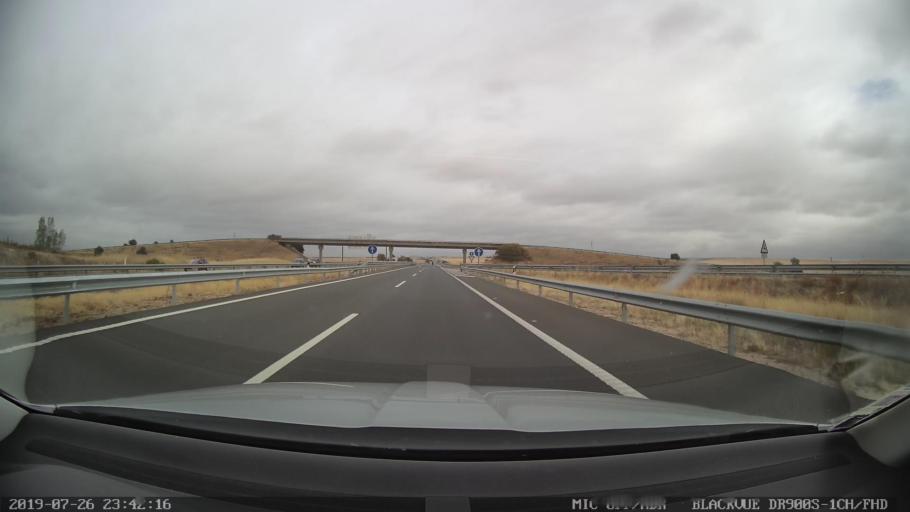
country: ES
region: Extremadura
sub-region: Provincia de Caceres
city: Trujillo
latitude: 39.5019
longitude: -5.8395
